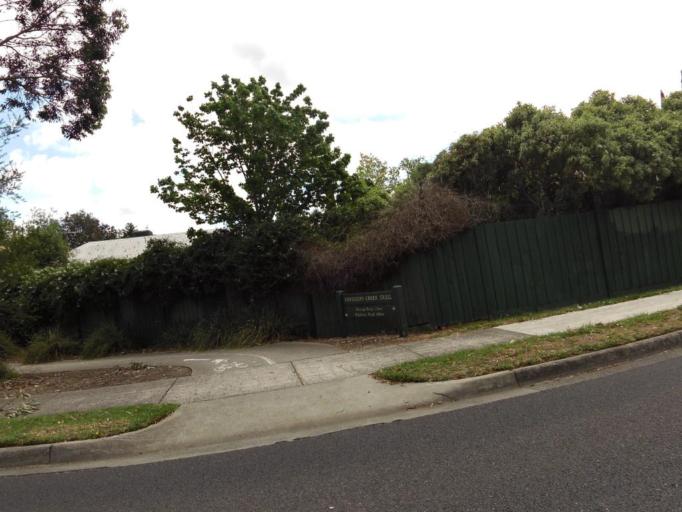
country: AU
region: Victoria
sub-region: Monash
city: Ashwood
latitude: -37.8667
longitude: 145.1008
